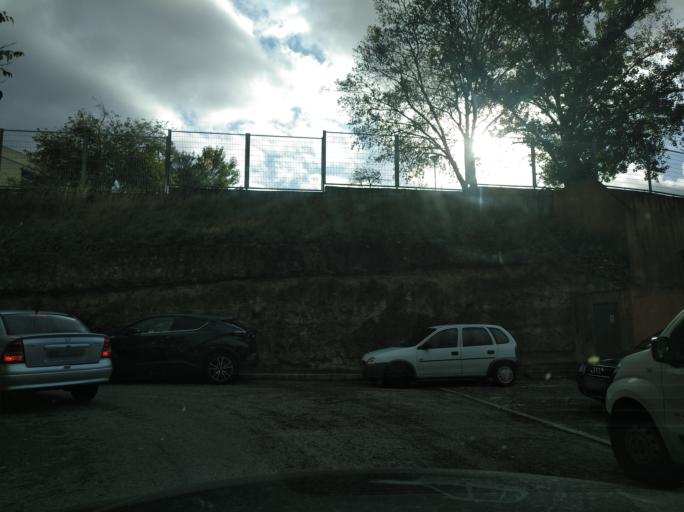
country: PT
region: Lisbon
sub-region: Loures
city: Sacavem
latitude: 38.7929
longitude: -9.1113
